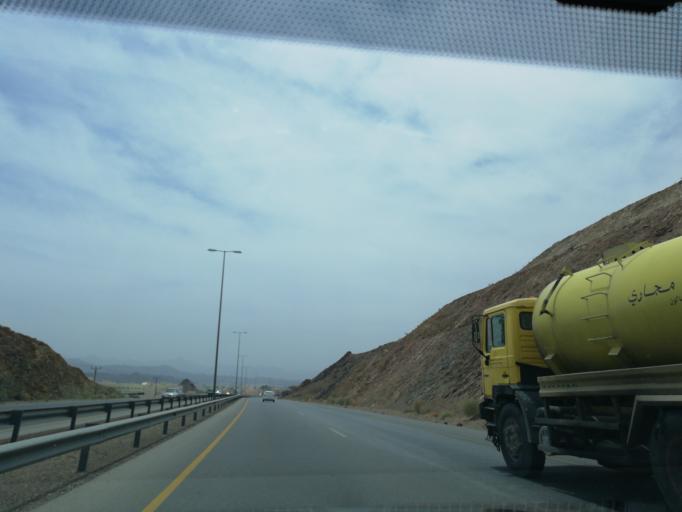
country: OM
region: Muhafazat ad Dakhiliyah
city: Sufalat Sama'il
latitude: 23.3063
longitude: 57.9425
